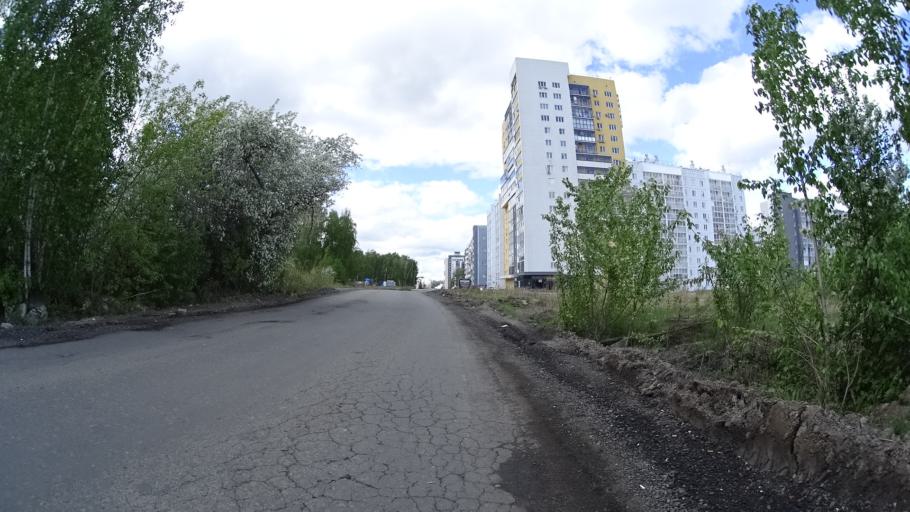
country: RU
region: Chelyabinsk
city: Sargazy
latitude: 55.1593
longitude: 61.2857
